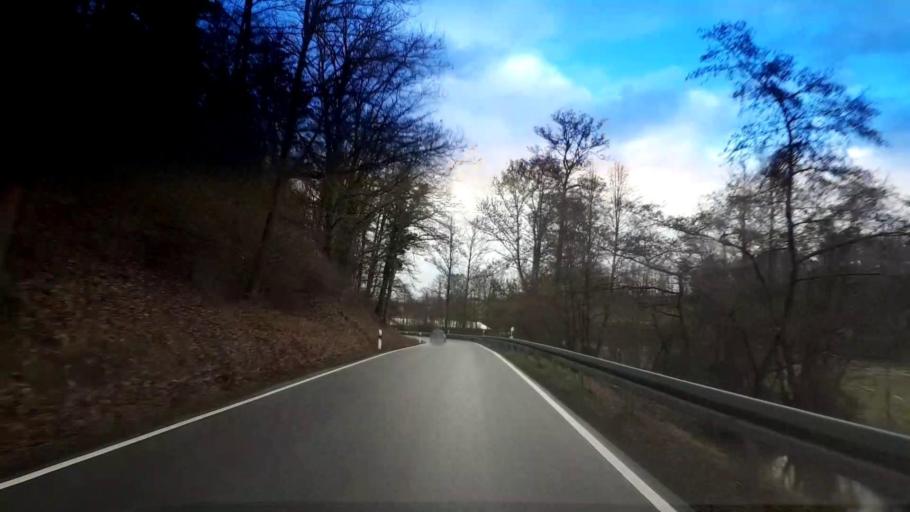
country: DE
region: Bavaria
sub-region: Upper Franconia
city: Lauter
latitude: 49.9734
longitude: 10.7812
